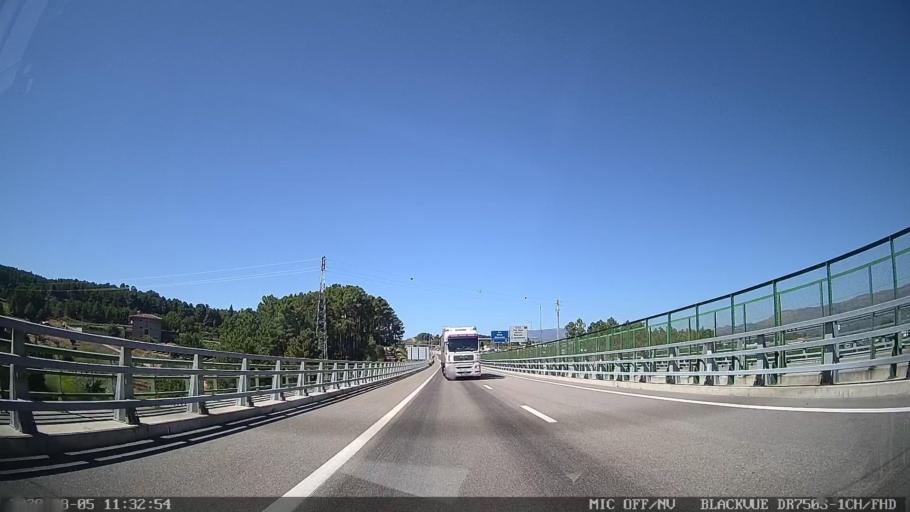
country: PT
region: Vila Real
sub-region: Vila Real
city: Vila Real
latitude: 41.2817
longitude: -7.7120
